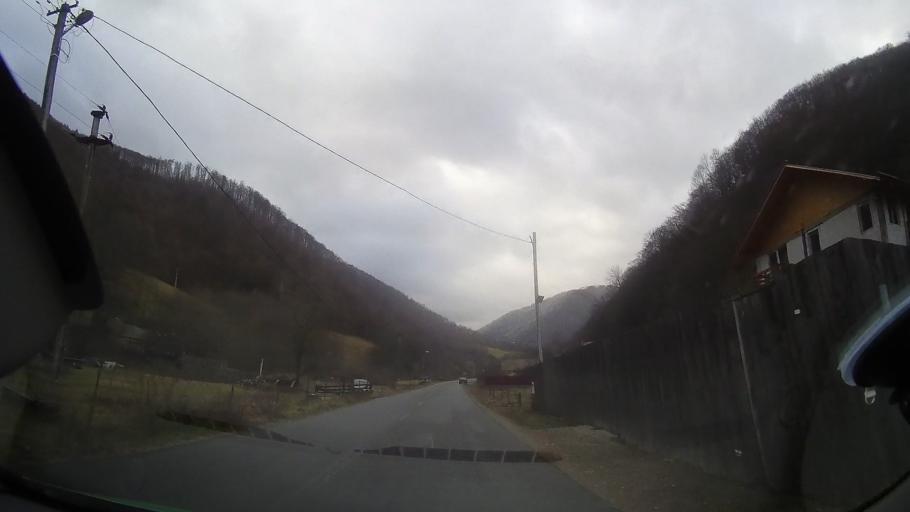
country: RO
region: Cluj
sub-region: Comuna Maguri-Racatau
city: Maguri-Racatau
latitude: 46.6575
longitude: 23.2144
